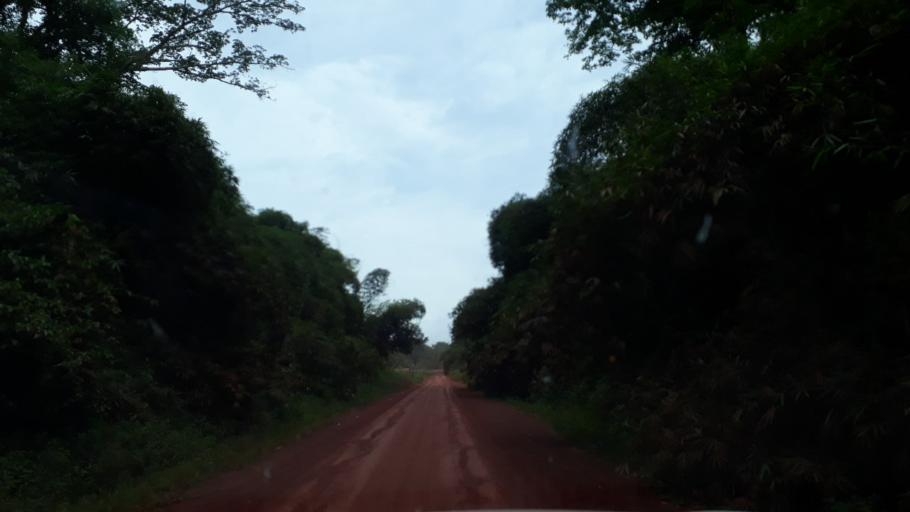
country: CD
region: Eastern Province
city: Kisangani
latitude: 0.5868
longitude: 25.9593
